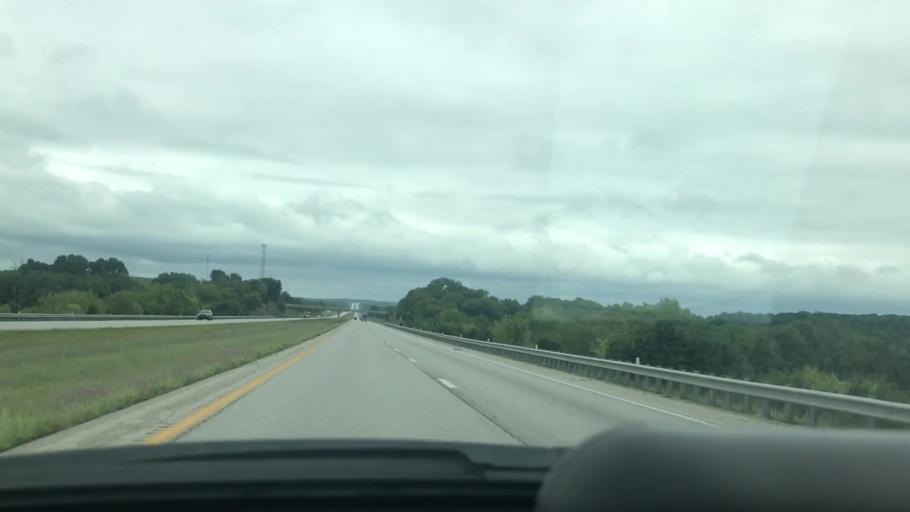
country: US
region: Missouri
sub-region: Lawrence County
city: Mount Vernon
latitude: 37.1518
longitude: -93.7012
